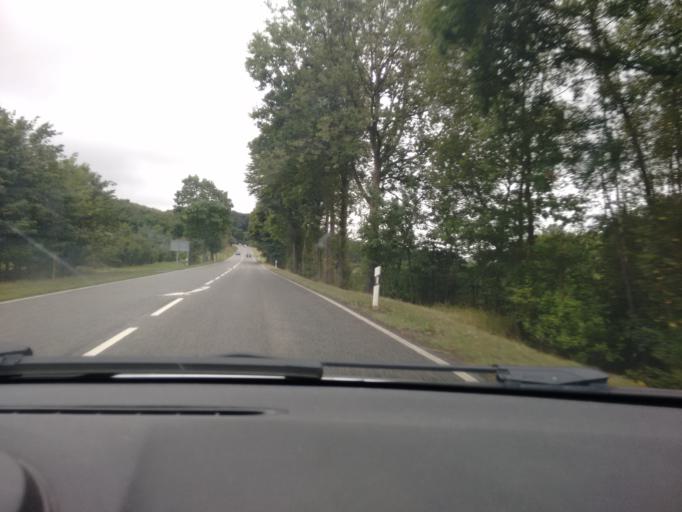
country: DE
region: Rheinland-Pfalz
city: Schmissberg
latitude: 49.6636
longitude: 7.1922
